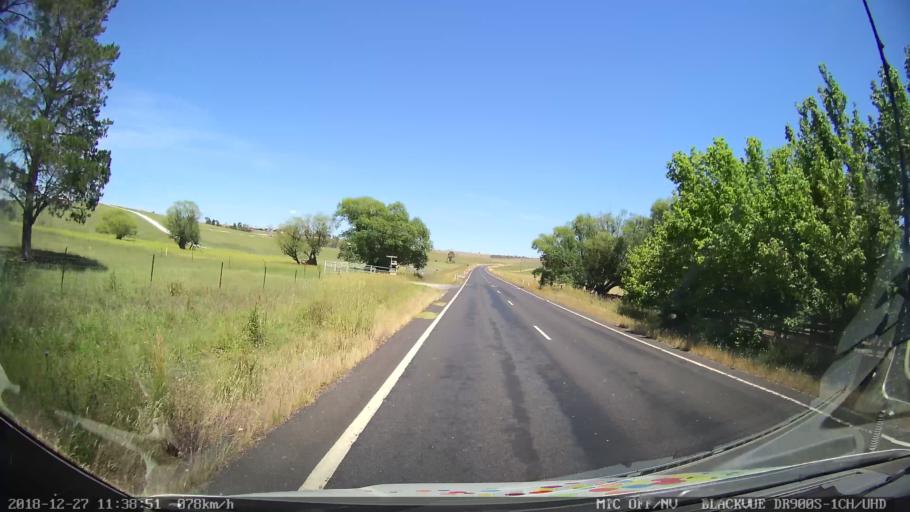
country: AU
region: New South Wales
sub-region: Bathurst Regional
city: Perthville
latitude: -33.5155
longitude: 149.5086
